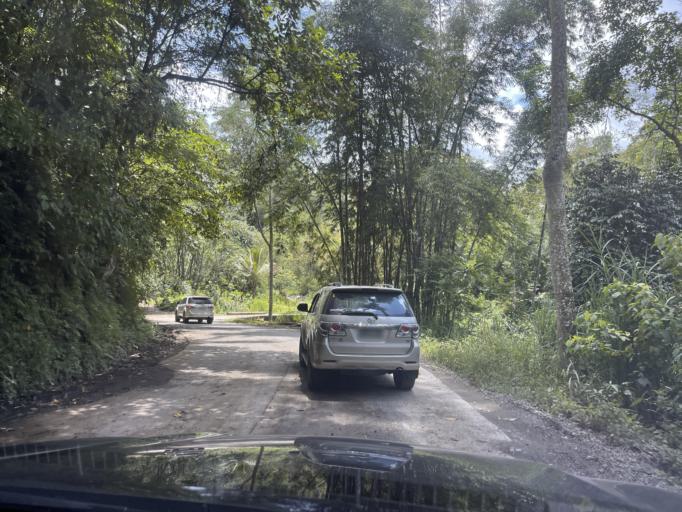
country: PH
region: Northern Mindanao
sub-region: Province of Bukidnon
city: Kisolon
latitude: 8.3111
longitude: 124.9644
